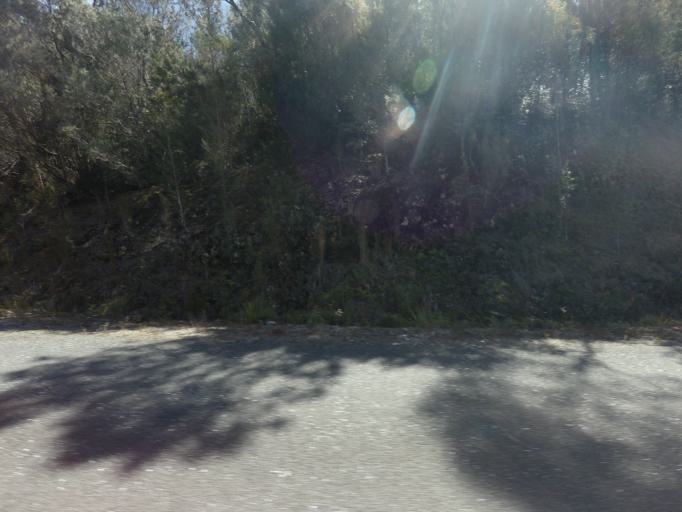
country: AU
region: Tasmania
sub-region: West Coast
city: Queenstown
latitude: -42.7761
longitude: 146.0373
